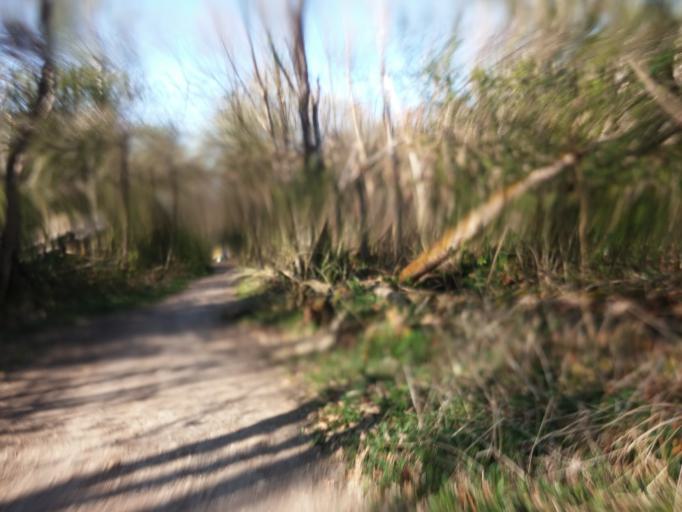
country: DE
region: Bavaria
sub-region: Upper Bavaria
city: Neubiberg
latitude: 48.1037
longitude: 11.6774
